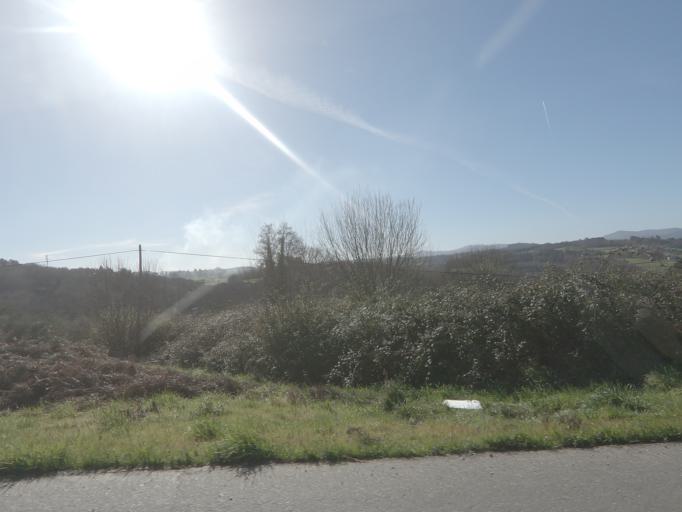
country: ES
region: Galicia
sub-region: Provincia de Pontevedra
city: Lalin
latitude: 42.6817
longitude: -8.1752
